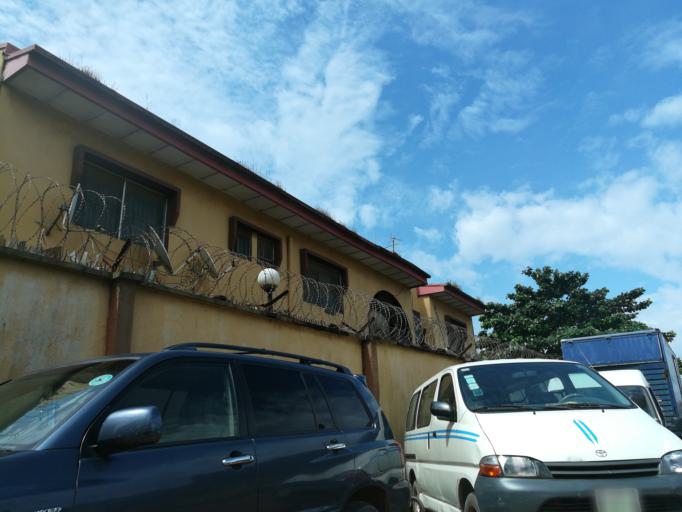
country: NG
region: Lagos
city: Agege
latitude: 6.6079
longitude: 3.3178
